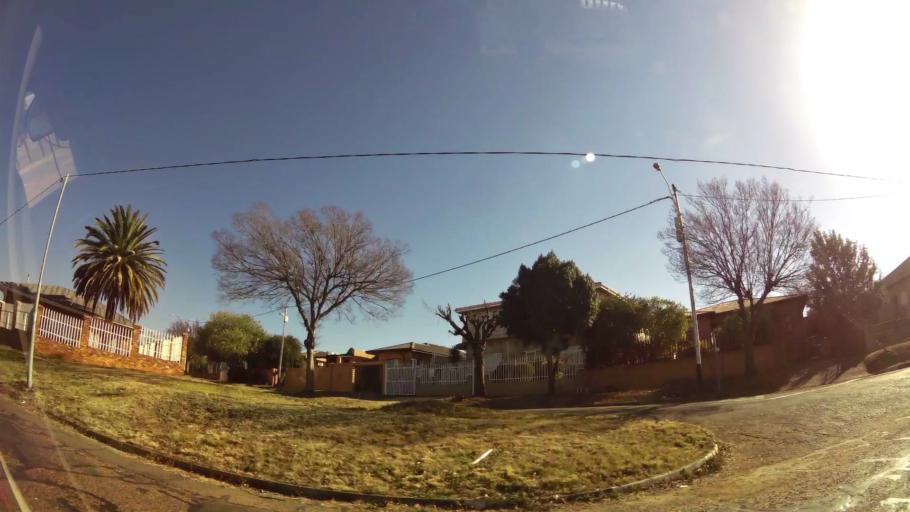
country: ZA
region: Gauteng
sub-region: City of Johannesburg Metropolitan Municipality
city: Johannesburg
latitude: -26.2005
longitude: 27.9976
